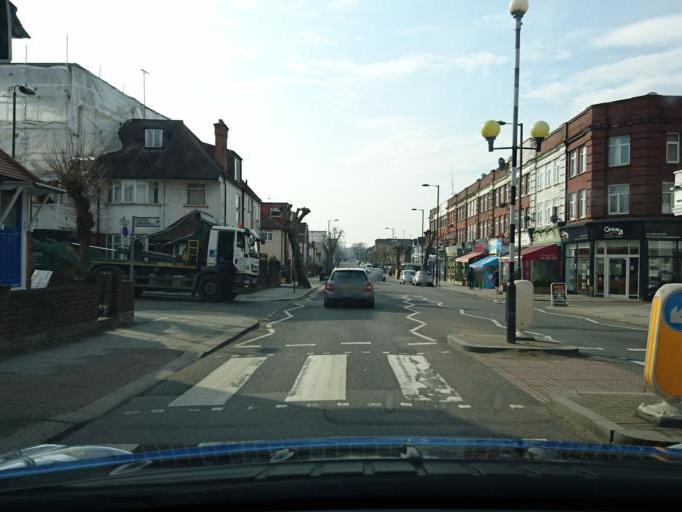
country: GB
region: England
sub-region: Greater London
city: Hendon
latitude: 51.5799
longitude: -0.1981
